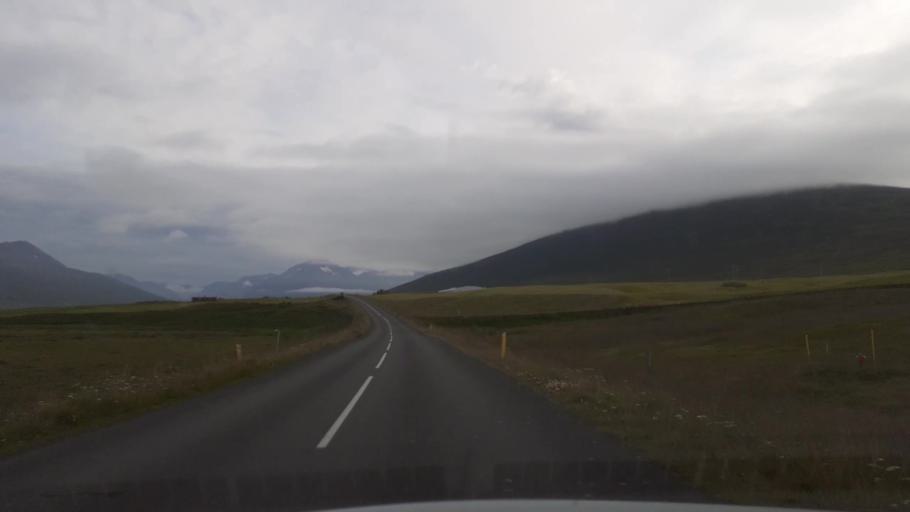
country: IS
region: Northeast
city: Dalvik
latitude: 65.9579
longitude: -18.5476
